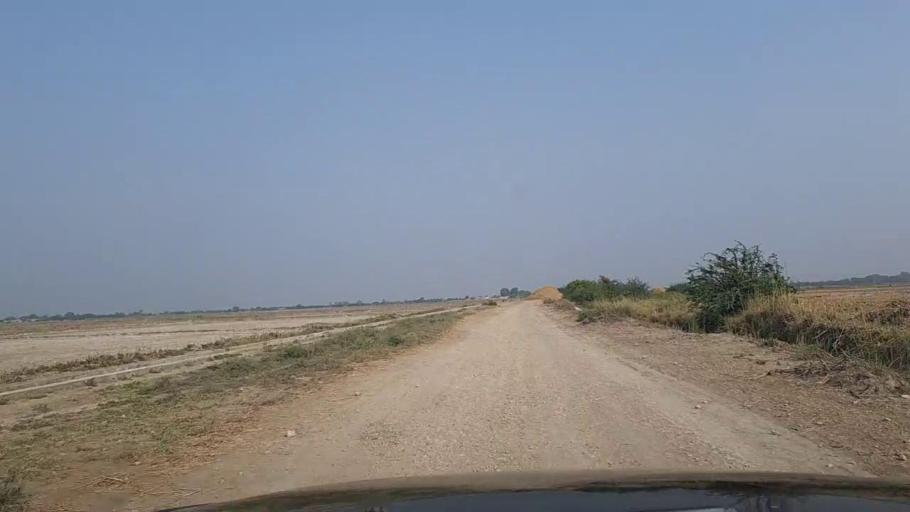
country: PK
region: Sindh
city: Thatta
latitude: 24.7598
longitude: 67.8716
